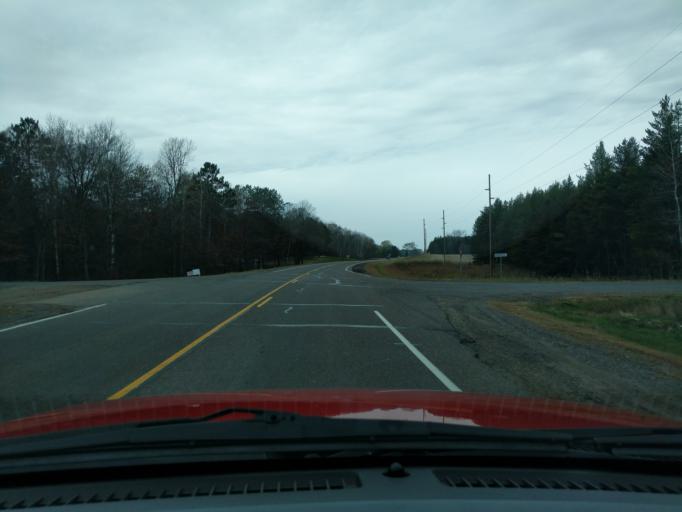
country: US
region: Wisconsin
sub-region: Washburn County
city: Spooner
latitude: 45.8152
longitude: -91.9701
